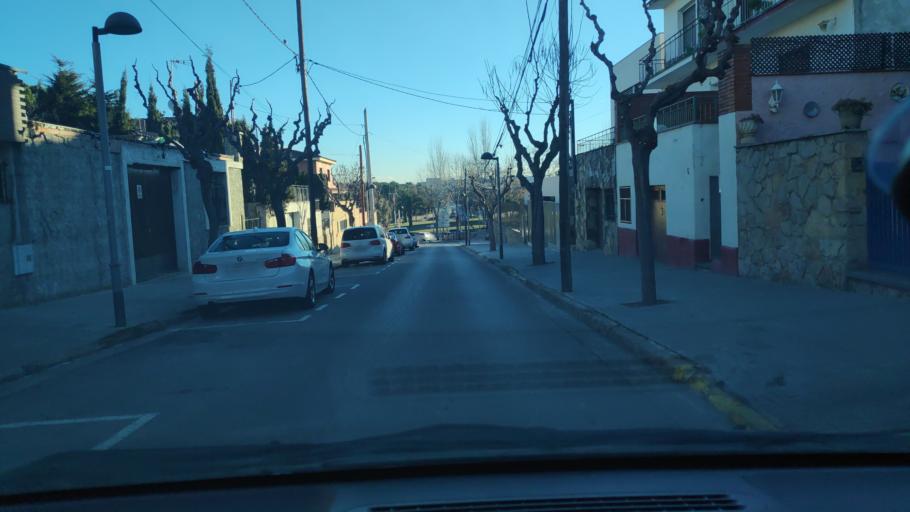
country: ES
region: Catalonia
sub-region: Provincia de Barcelona
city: Sant Quirze del Valles
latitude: 41.5301
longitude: 2.0850
